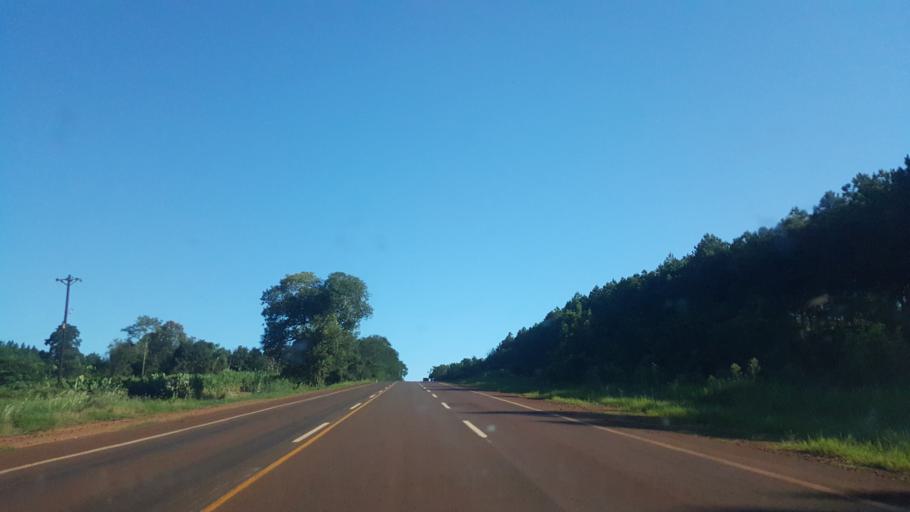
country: AR
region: Misiones
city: Puerto Esperanza
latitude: -26.1570
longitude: -54.5832
